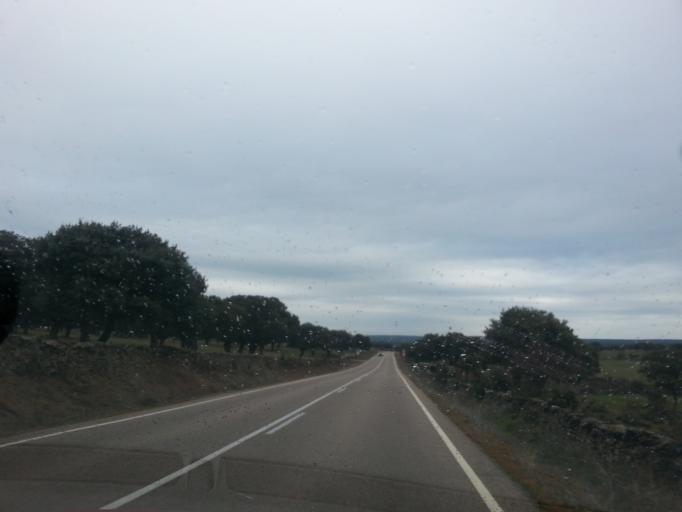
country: ES
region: Castille and Leon
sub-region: Provincia de Salamanca
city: Narros de Matalayegua
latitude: 40.7366
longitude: -5.9328
